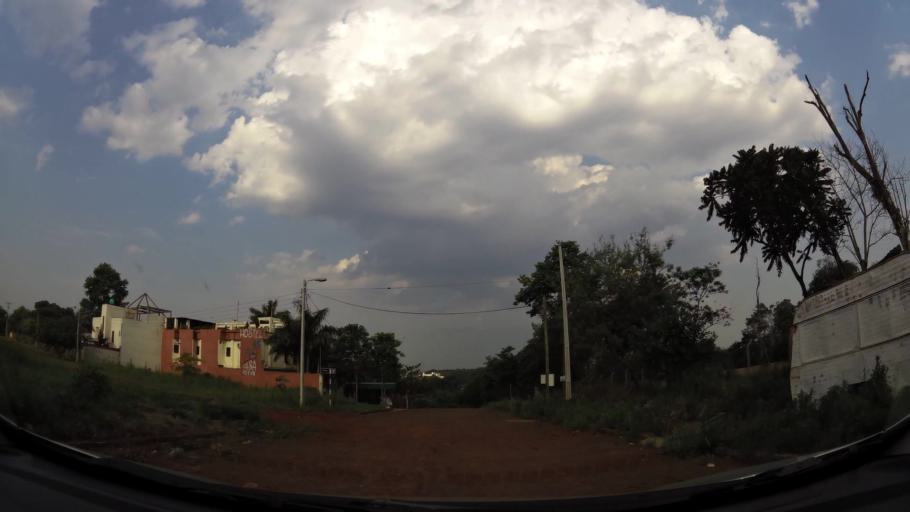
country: PY
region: Alto Parana
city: Presidente Franco
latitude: -25.5220
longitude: -54.6272
